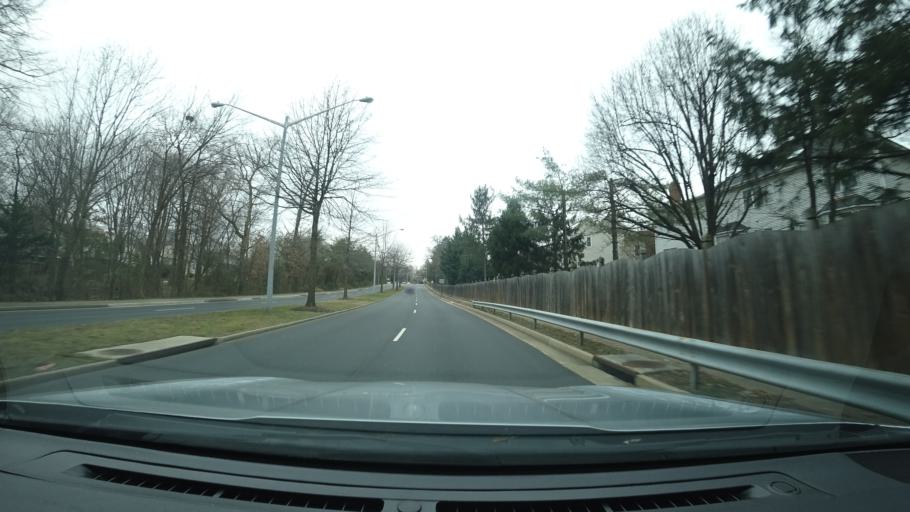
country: US
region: Virginia
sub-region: Fairfax County
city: Herndon
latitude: 38.9825
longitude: -77.3751
